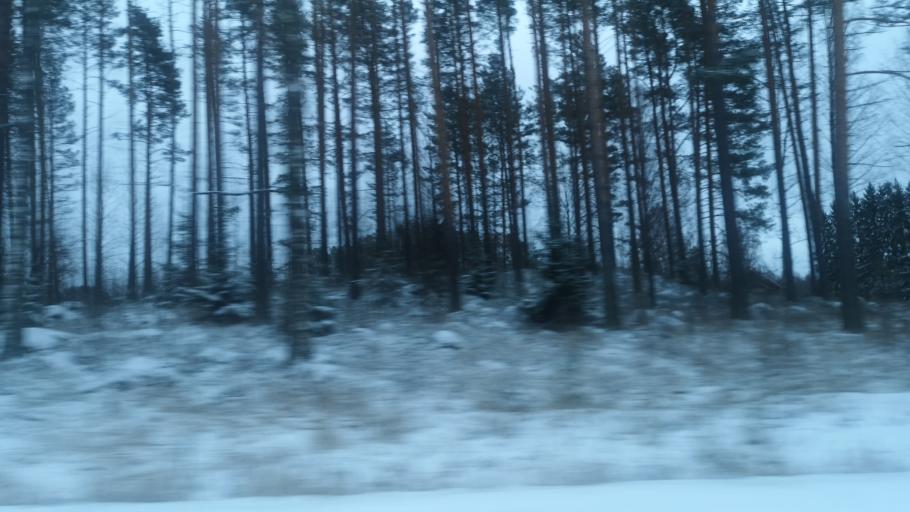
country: FI
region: Southern Savonia
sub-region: Savonlinna
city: Savonlinna
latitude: 62.0199
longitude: 28.7285
